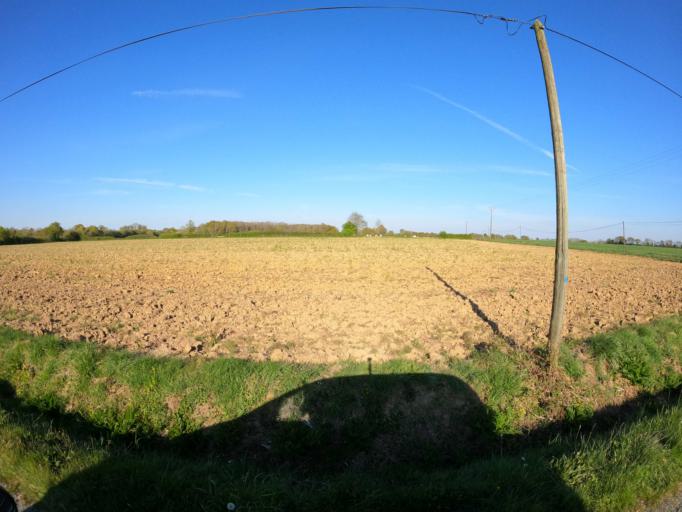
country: FR
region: Pays de la Loire
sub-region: Departement de la Vendee
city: Les Brouzils
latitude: 46.8922
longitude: -1.3671
